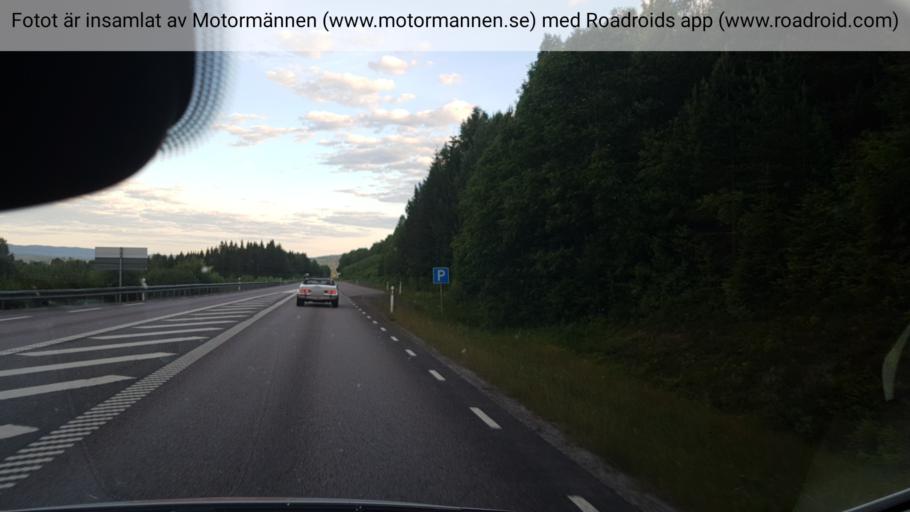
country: SE
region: Vaermland
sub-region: Sunne Kommun
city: Sunne
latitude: 59.9836
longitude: 13.1016
